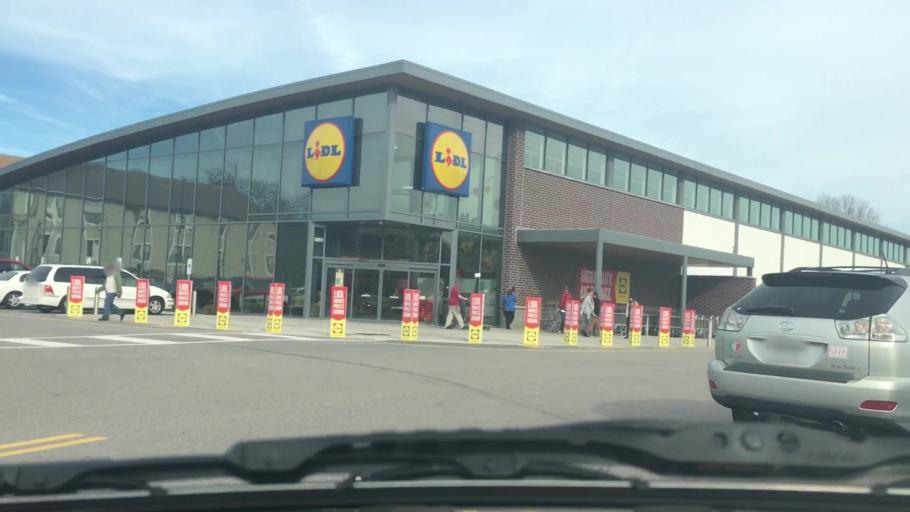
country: US
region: Virginia
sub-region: City of Norfolk
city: Norfolk
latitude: 36.8999
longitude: -76.2270
